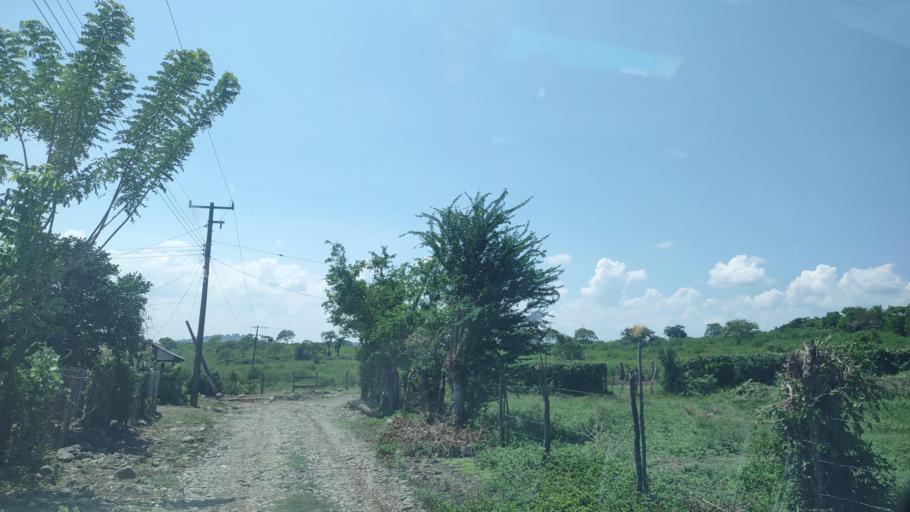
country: MX
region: Veracruz
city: Los Altos
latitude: 21.4317
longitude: -97.7913
